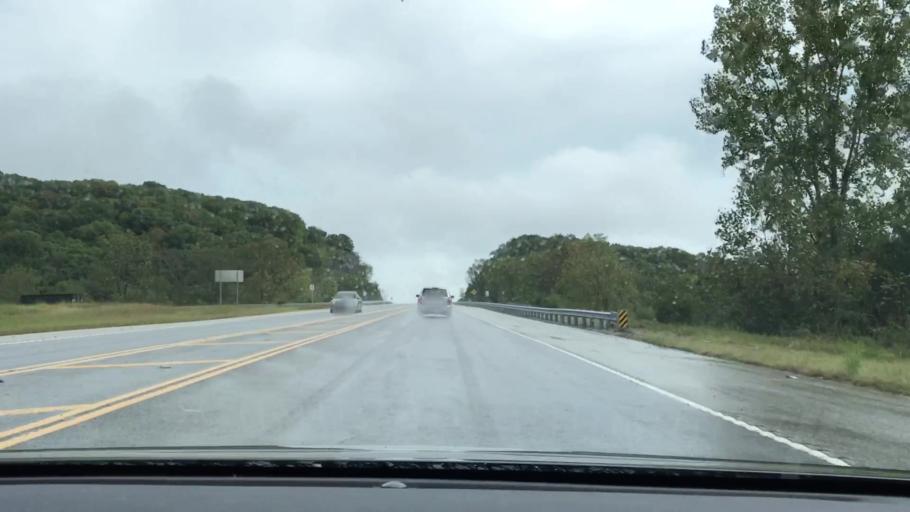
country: US
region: Tennessee
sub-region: Smith County
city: Carthage
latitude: 36.2613
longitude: -85.9461
